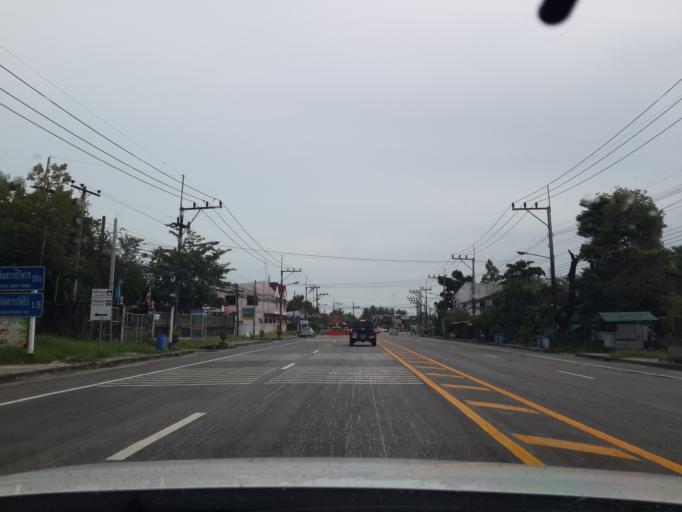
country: TH
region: Pattani
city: Nong Chik
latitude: 6.8431
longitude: 101.1772
